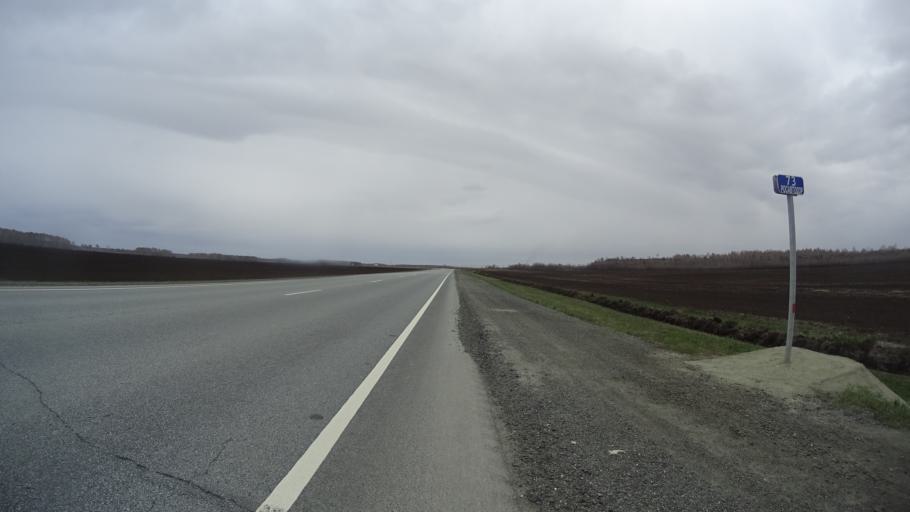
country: RU
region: Chelyabinsk
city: Krasnogorskiy
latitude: 54.5720
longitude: 61.2907
